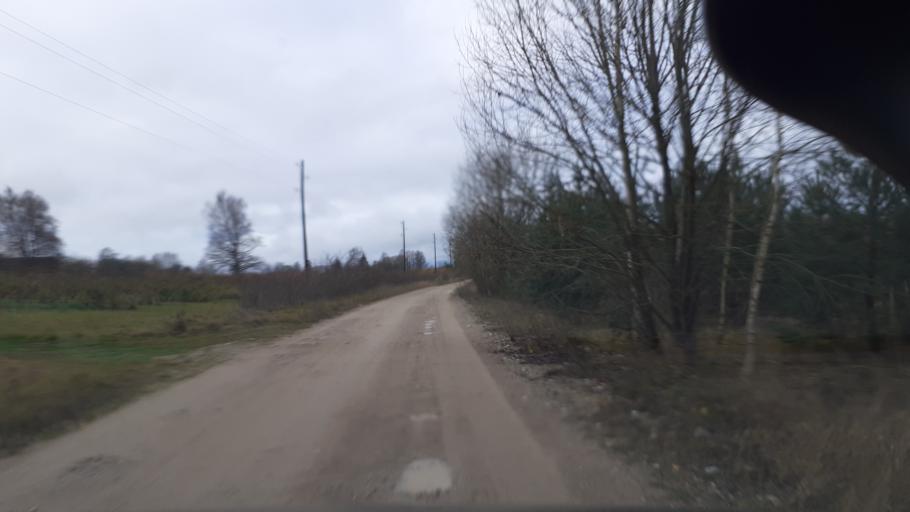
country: LV
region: Kuldigas Rajons
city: Kuldiga
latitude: 57.0402
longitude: 21.8784
